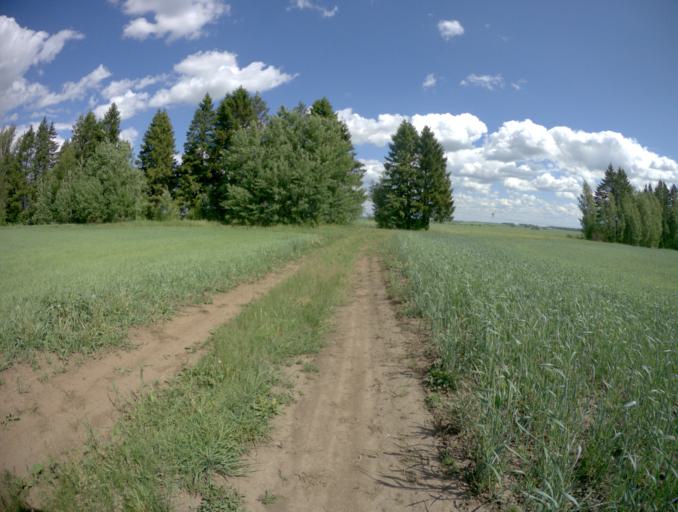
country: RU
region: Vladimir
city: Suzdal'
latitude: 56.4351
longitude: 40.3497
